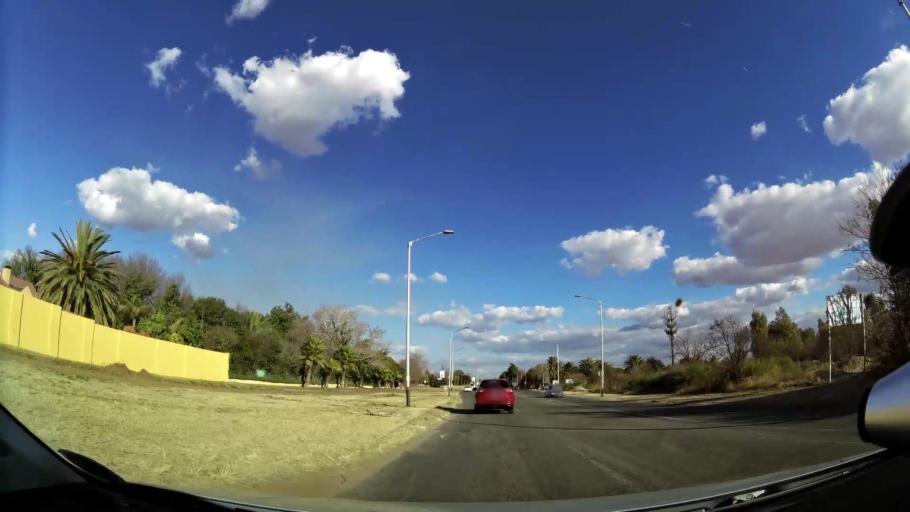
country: ZA
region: North-West
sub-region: Dr Kenneth Kaunda District Municipality
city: Klerksdorp
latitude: -26.8488
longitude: 26.6636
